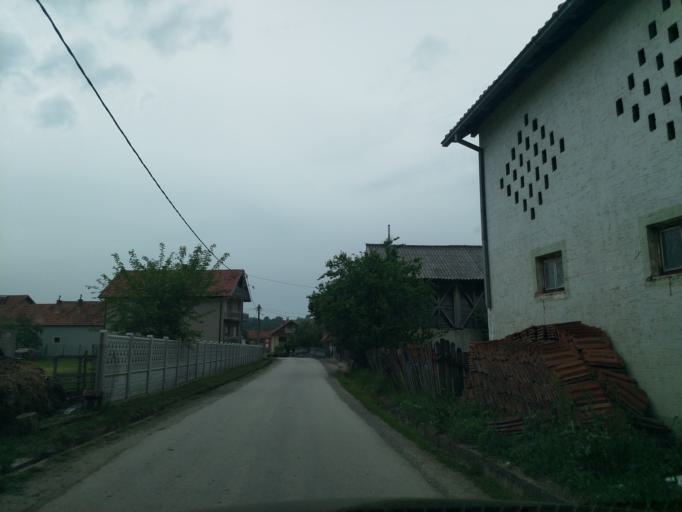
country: RS
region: Central Serbia
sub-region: Pomoravski Okrug
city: Paracin
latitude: 43.8786
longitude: 21.5668
